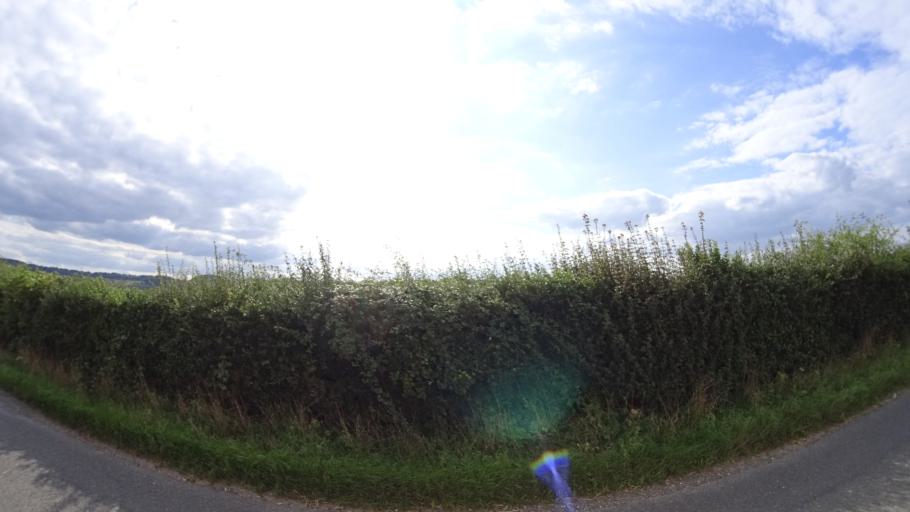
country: GB
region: England
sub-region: Hampshire
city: East Dean
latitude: 51.1088
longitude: -1.5759
